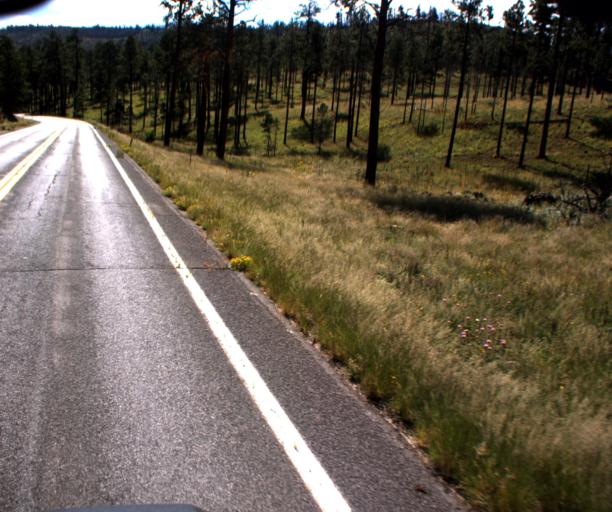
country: US
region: Arizona
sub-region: Apache County
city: Eagar
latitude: 34.0500
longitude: -109.3556
